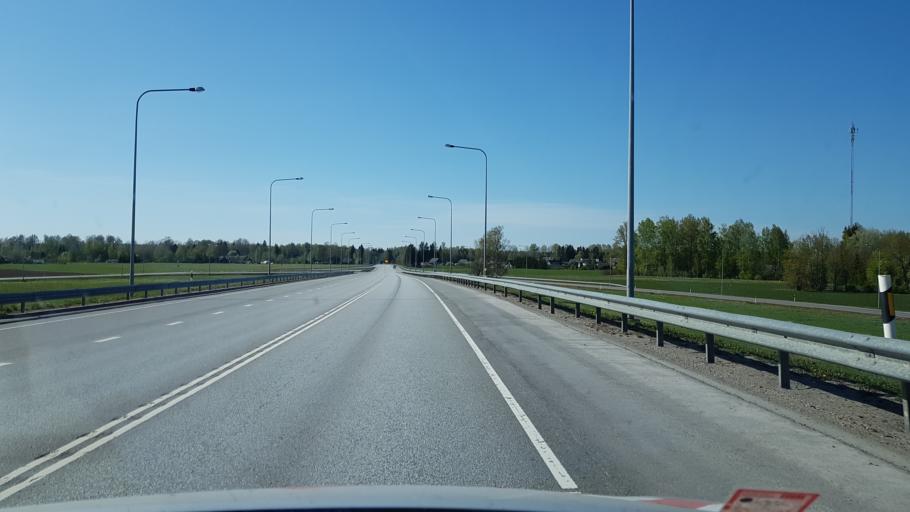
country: EE
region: Jogevamaa
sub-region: Jogeva linn
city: Jogeva
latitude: 58.5711
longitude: 26.2854
